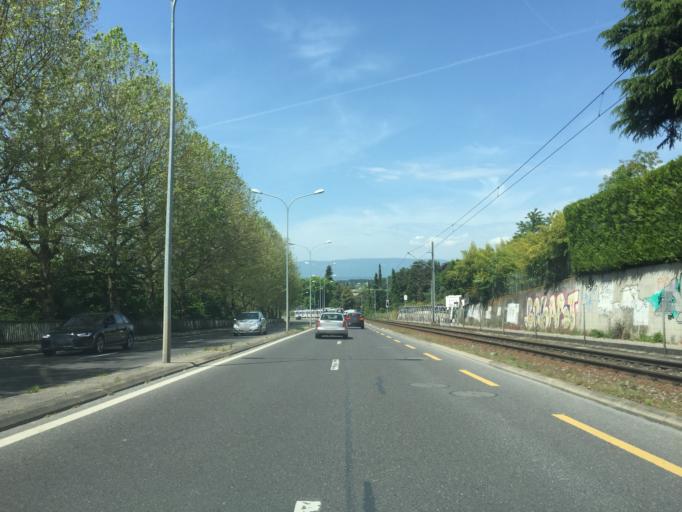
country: CH
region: Vaud
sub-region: Ouest Lausannois District
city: Prilly
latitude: 46.5238
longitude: 6.5971
